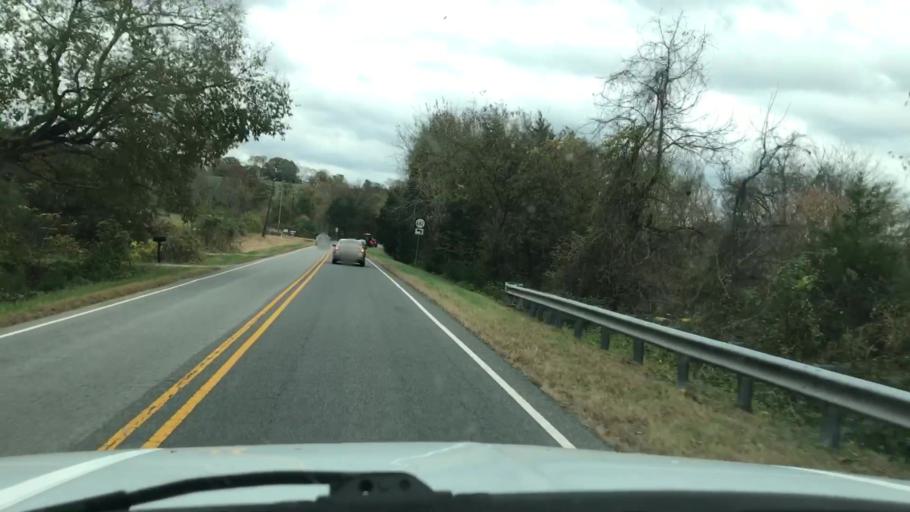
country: US
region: Virginia
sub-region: Goochland County
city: Goochland
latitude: 37.6215
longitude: -77.7714
